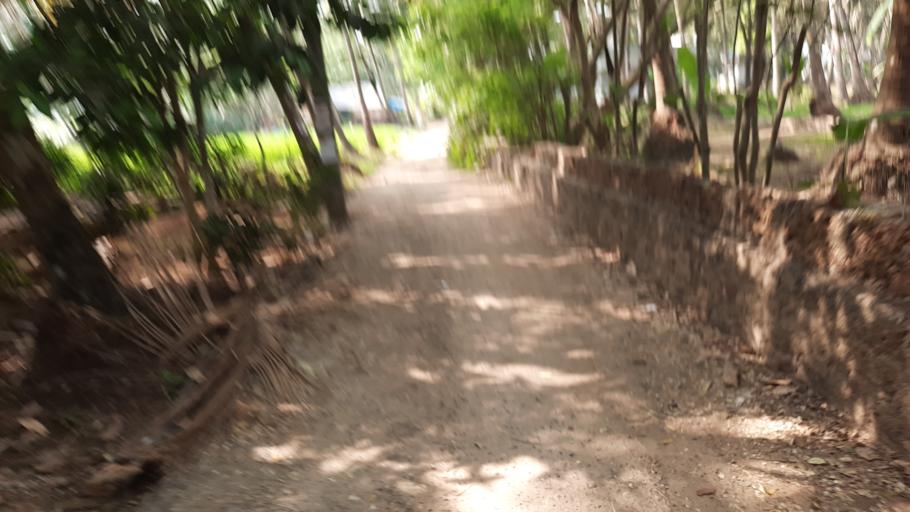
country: IN
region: Kerala
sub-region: Malappuram
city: Ponnani
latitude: 10.8307
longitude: 75.9458
